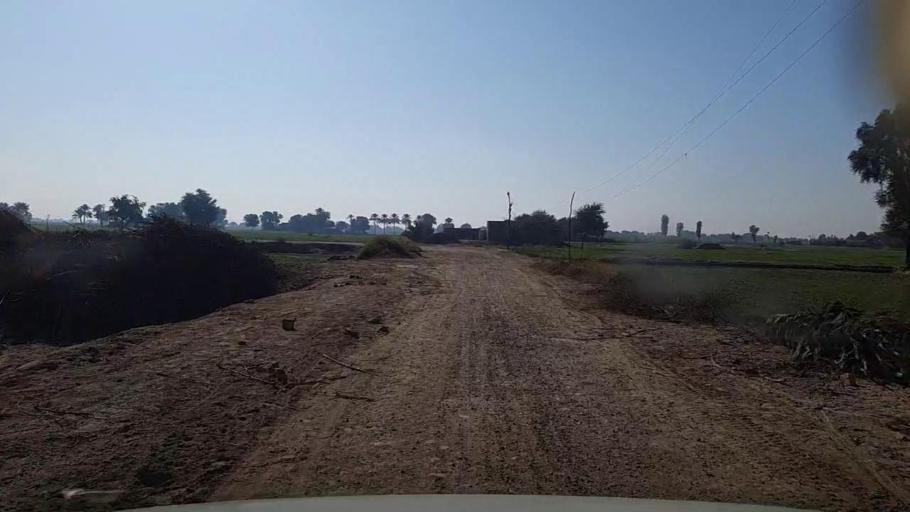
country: PK
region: Sindh
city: Khairpur
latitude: 28.0522
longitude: 69.7424
